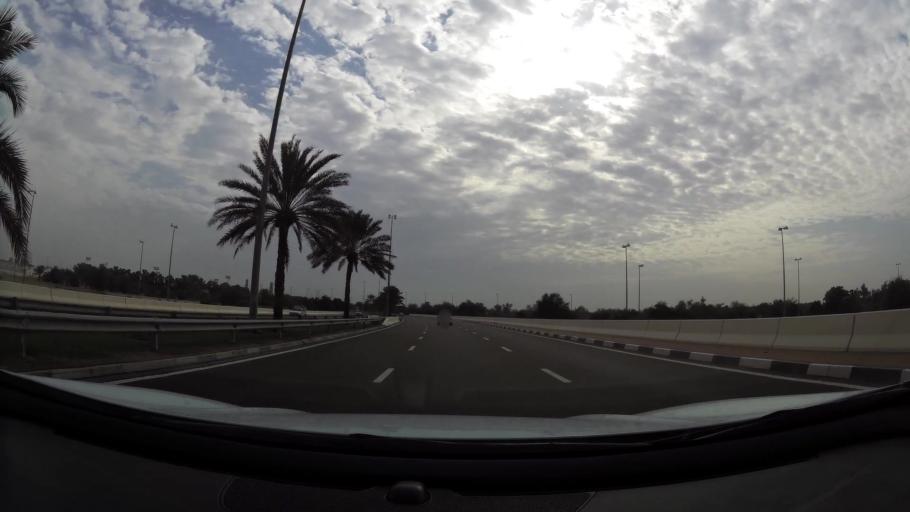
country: AE
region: Abu Dhabi
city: Al Ain
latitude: 24.1763
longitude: 55.6052
